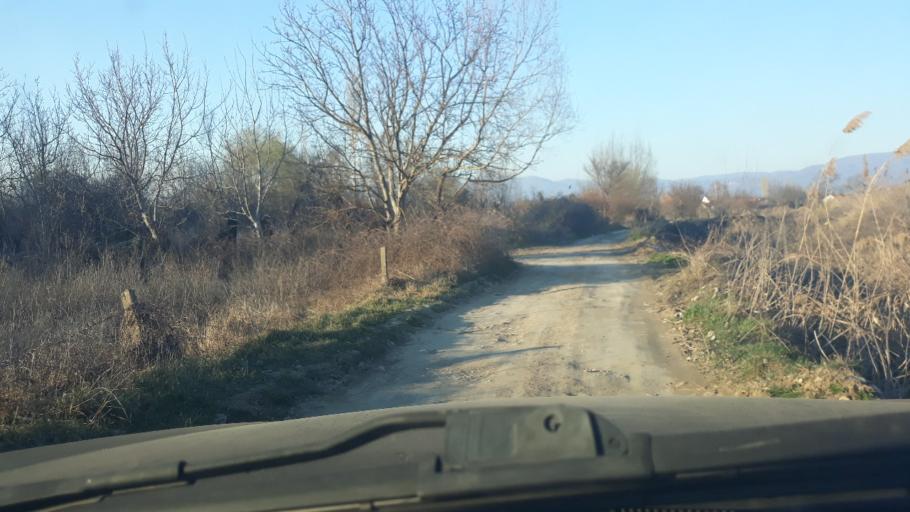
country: MK
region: Strumica
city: Strumica
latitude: 41.4423
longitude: 22.6264
